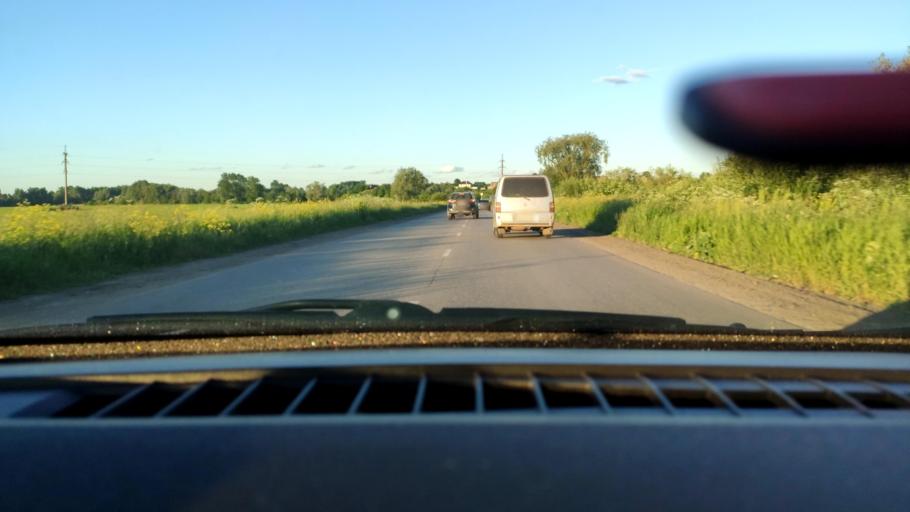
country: RU
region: Perm
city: Kultayevo
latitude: 57.9282
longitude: 55.9973
